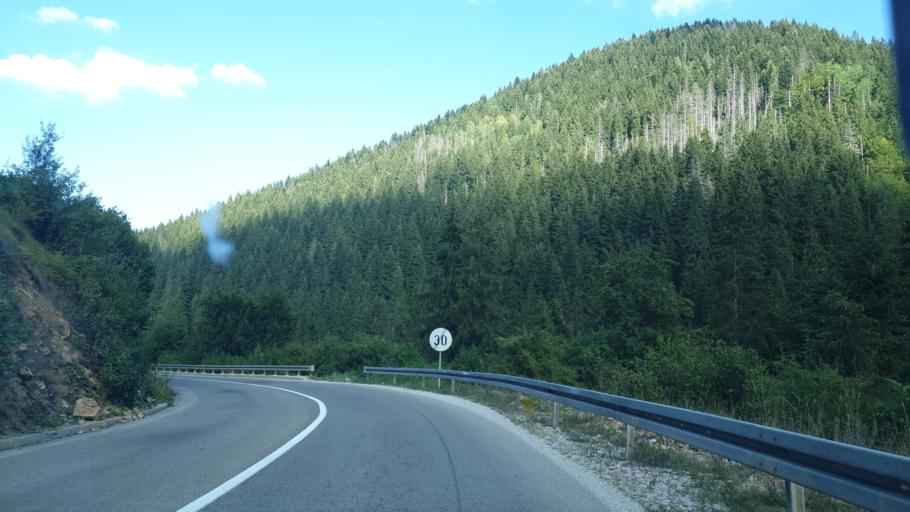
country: RS
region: Central Serbia
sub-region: Zlatiborski Okrug
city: Nova Varos
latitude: 43.4656
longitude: 19.8349
